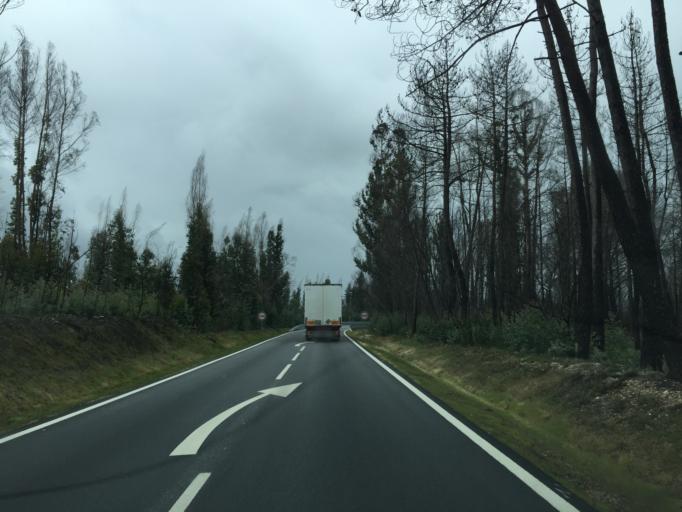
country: PT
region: Coimbra
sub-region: Oliveira do Hospital
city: Oliveira do Hospital
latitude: 40.3272
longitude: -7.9384
